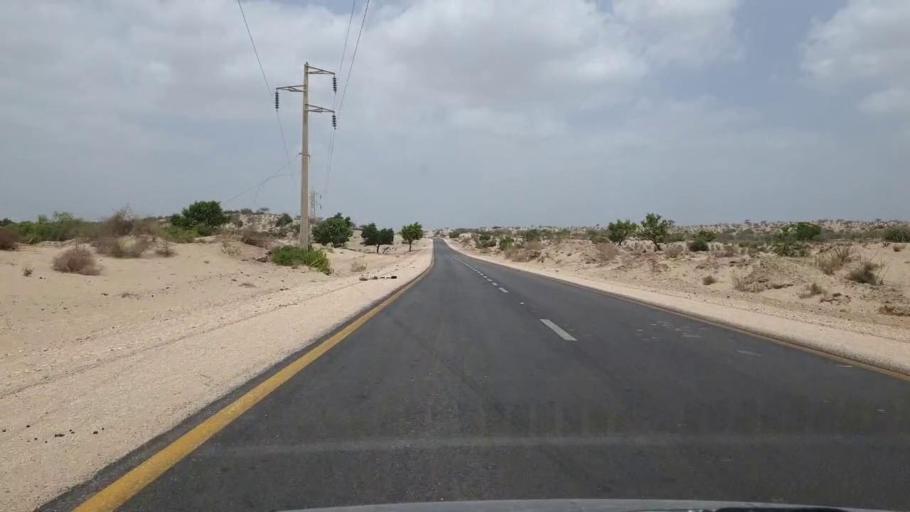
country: PK
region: Sindh
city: Naukot
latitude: 24.8464
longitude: 69.5289
